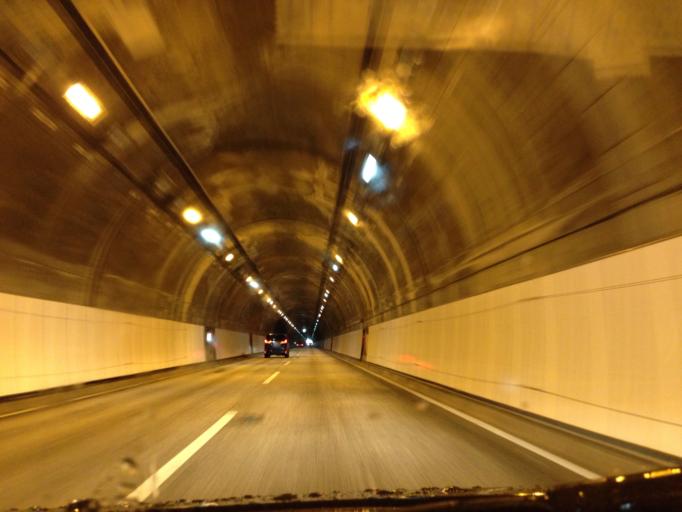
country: JP
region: Kanagawa
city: Odawara
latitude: 35.2492
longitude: 139.1331
